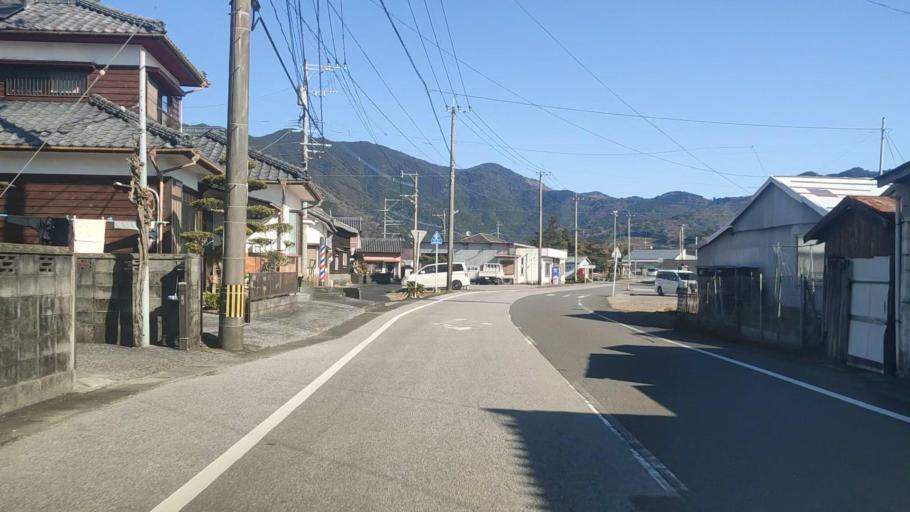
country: JP
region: Oita
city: Saiki
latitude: 32.8044
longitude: 131.8891
